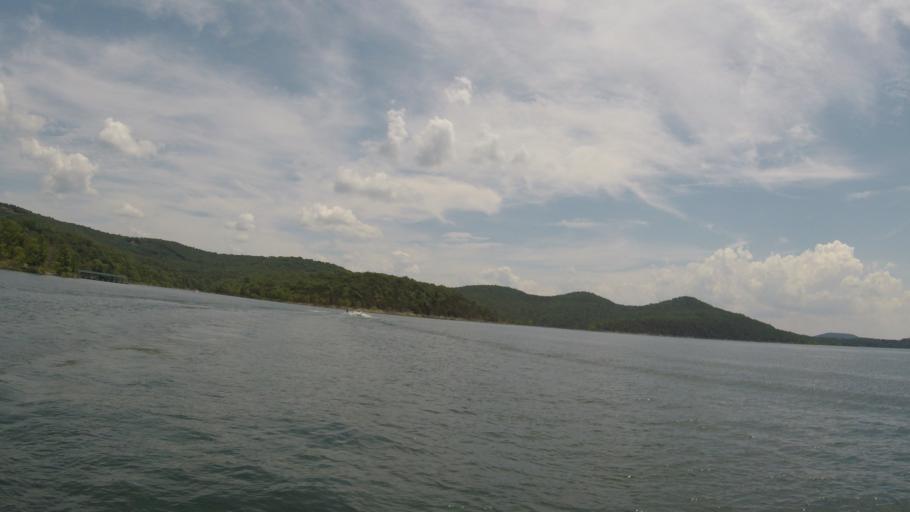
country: US
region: Missouri
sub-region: Barry County
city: Shell Knob
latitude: 36.6177
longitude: -93.5399
